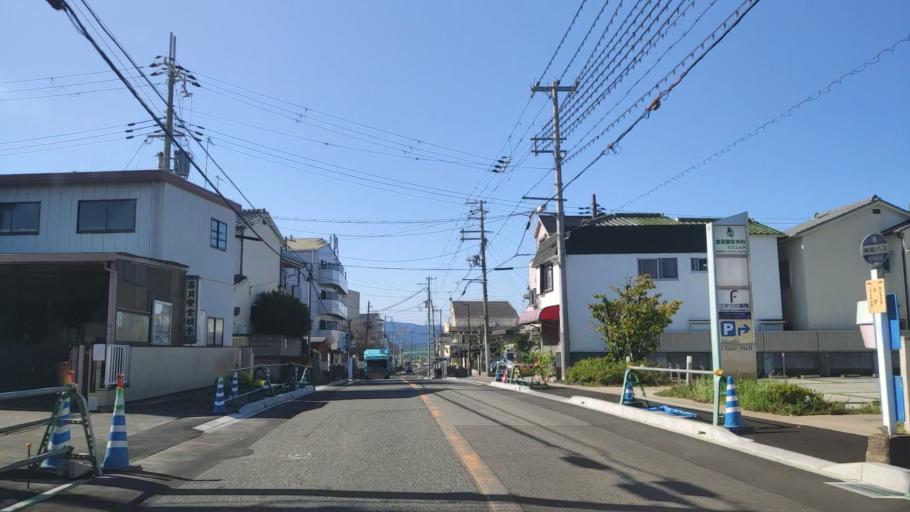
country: JP
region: Hyogo
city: Akashi
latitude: 34.6531
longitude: 135.0069
